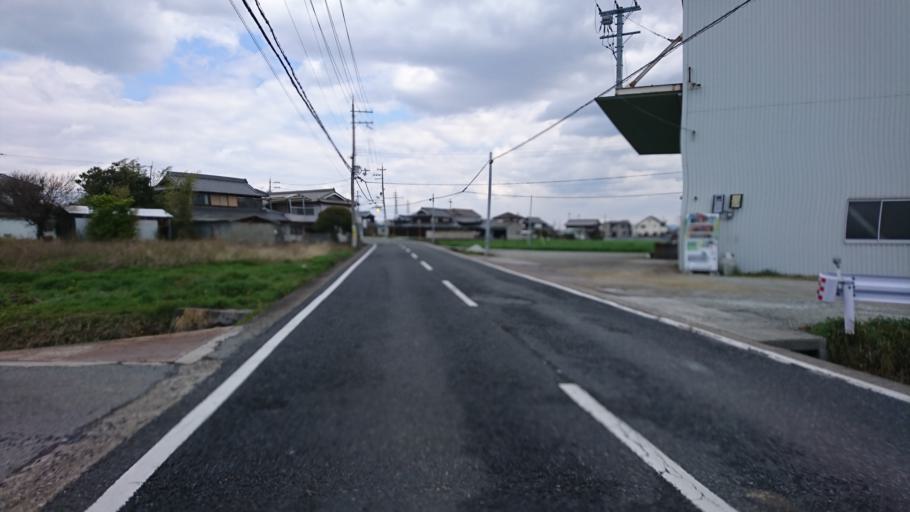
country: JP
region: Hyogo
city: Miki
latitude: 34.7373
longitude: 134.9273
